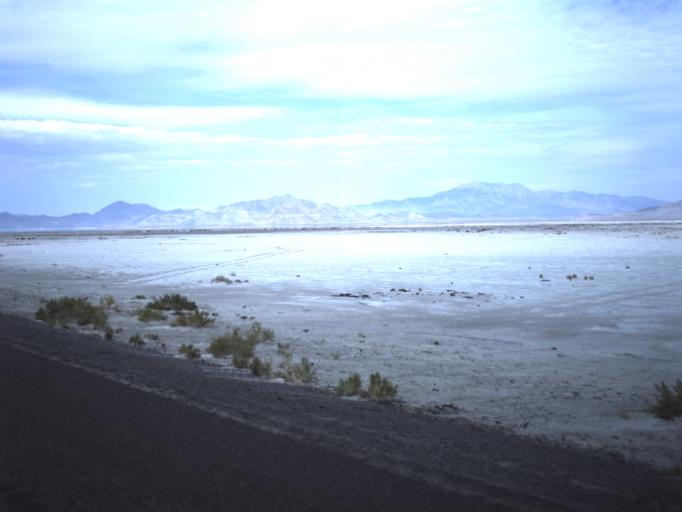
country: US
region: Utah
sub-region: Tooele County
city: Wendover
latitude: 40.7369
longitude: -113.7283
